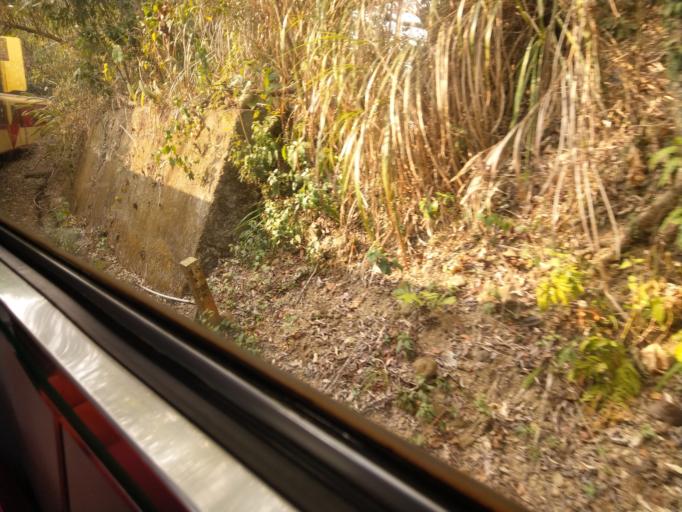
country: TW
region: Taiwan
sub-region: Chiayi
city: Jiayi Shi
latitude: 23.5372
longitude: 120.5765
